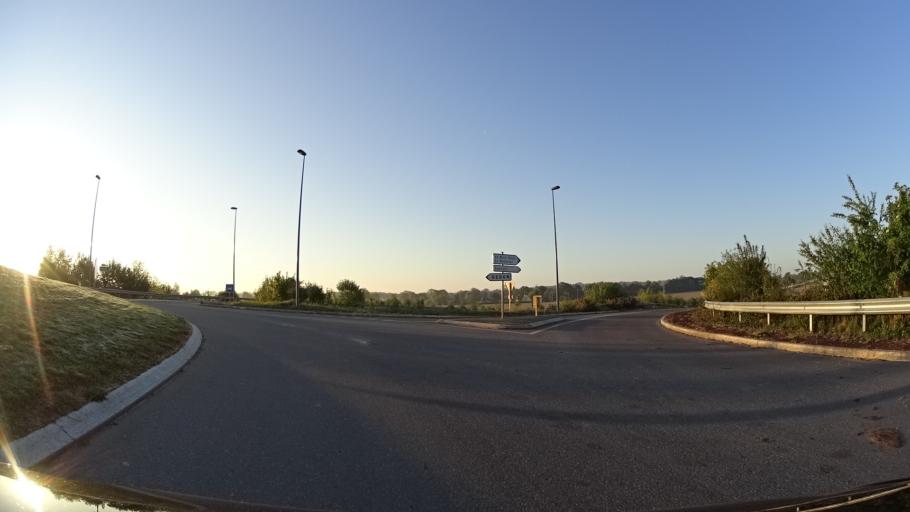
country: FR
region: Brittany
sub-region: Departement d'Ille-et-Vilaine
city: Pipriac
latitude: 47.8357
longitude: -1.9076
